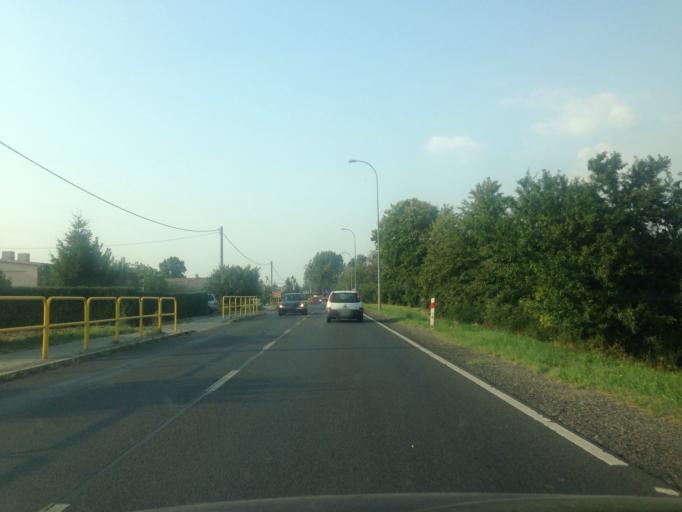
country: PL
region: Kujawsko-Pomorskie
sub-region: Powiat wloclawski
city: Fabianki
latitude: 52.7202
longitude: 19.1101
